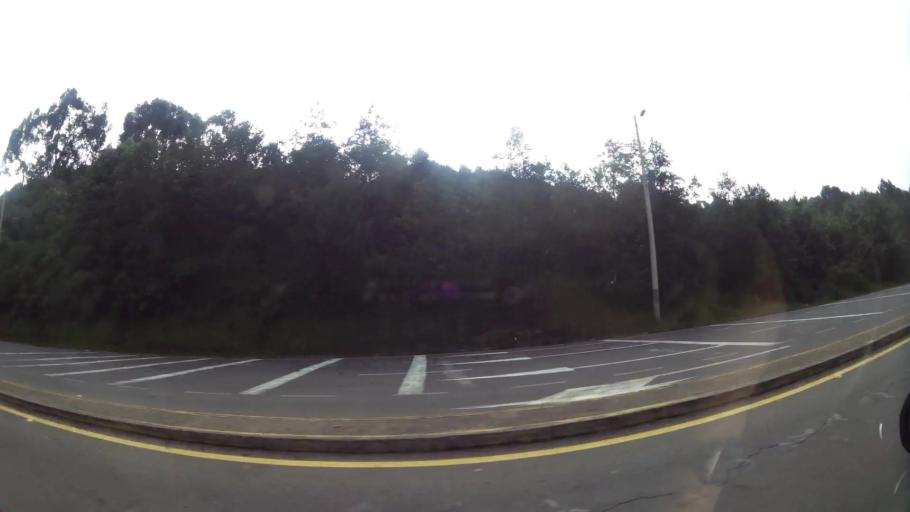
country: EC
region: Pichincha
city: Sangolqui
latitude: -0.3331
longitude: -78.5197
